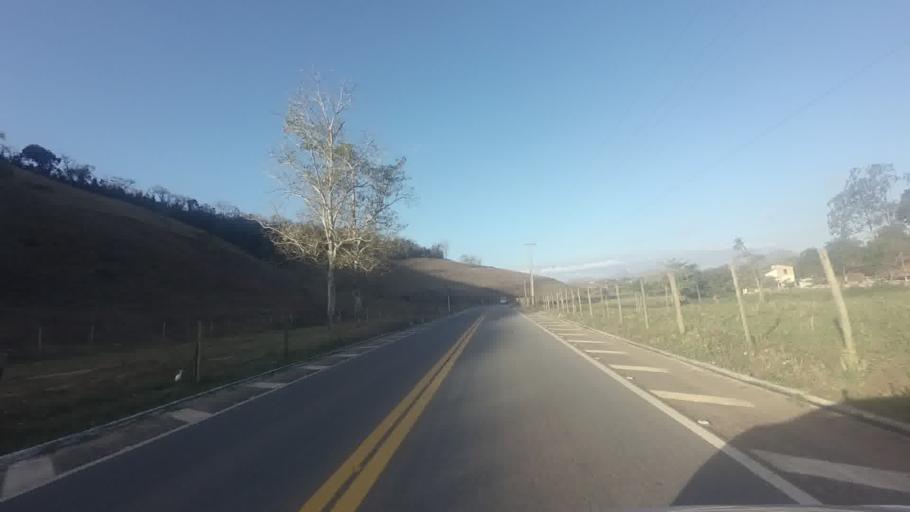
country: BR
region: Espirito Santo
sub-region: Cachoeiro De Itapemirim
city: Cachoeiro de Itapemirim
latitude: -20.8269
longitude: -41.1890
